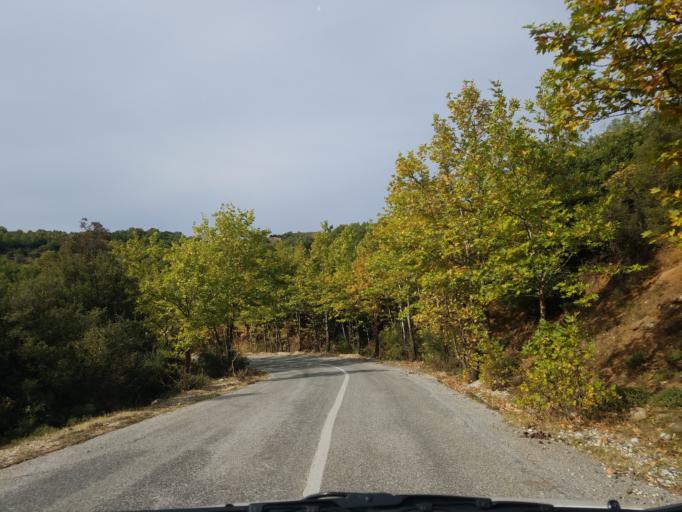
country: GR
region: Thessaly
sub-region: Trikala
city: Kalampaka
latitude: 39.7240
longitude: 21.6475
